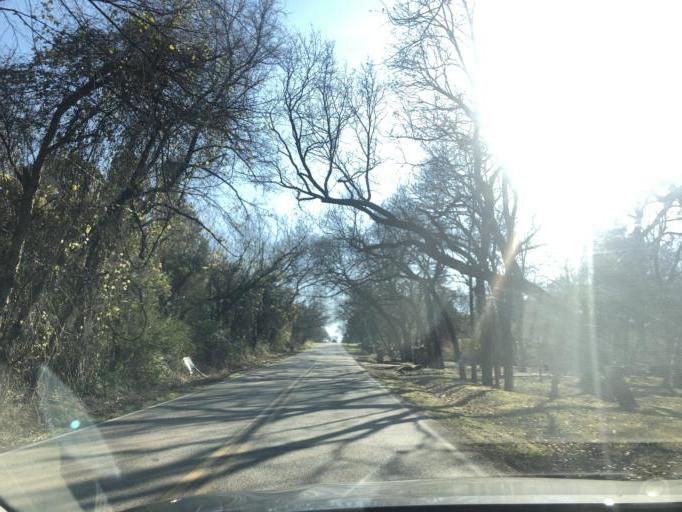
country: US
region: Texas
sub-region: Dallas County
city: Duncanville
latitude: 32.6232
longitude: -96.9255
